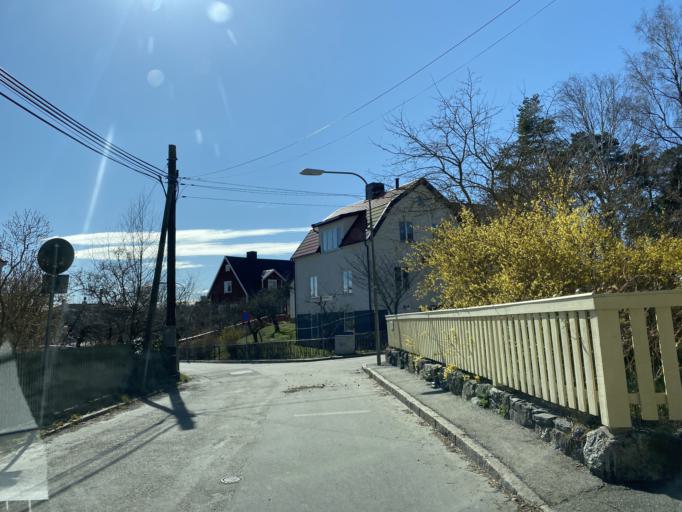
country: SE
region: Stockholm
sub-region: Stockholms Kommun
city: Arsta
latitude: 59.2816
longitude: 18.0554
